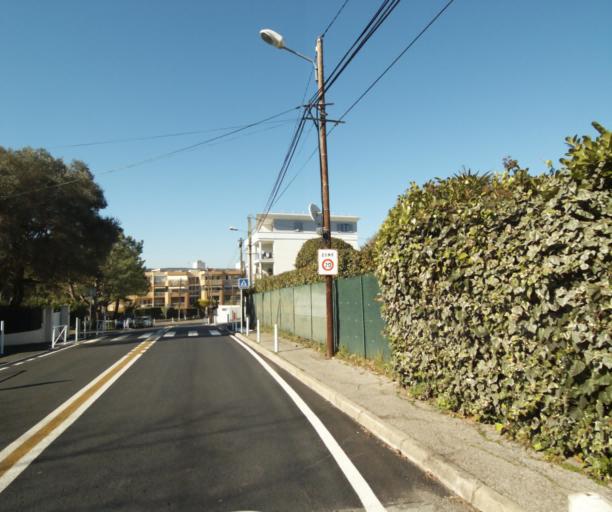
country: FR
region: Provence-Alpes-Cote d'Azur
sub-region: Departement des Alpes-Maritimes
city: Biot
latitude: 43.5974
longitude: 7.0954
